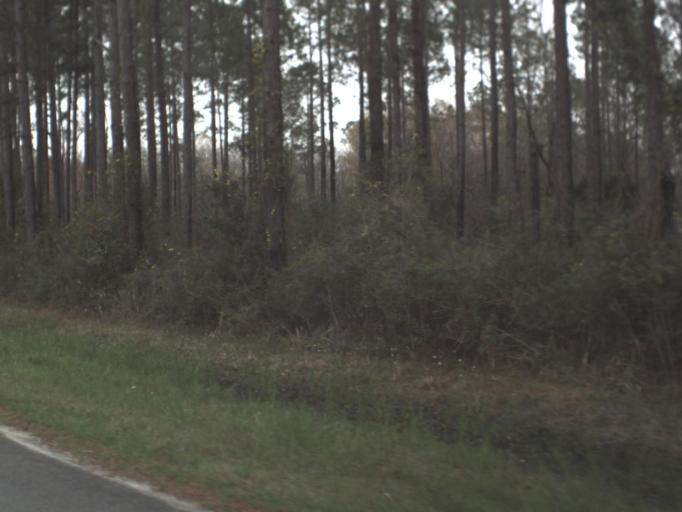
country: US
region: Florida
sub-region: Leon County
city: Woodville
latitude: 30.1934
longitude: -84.2047
